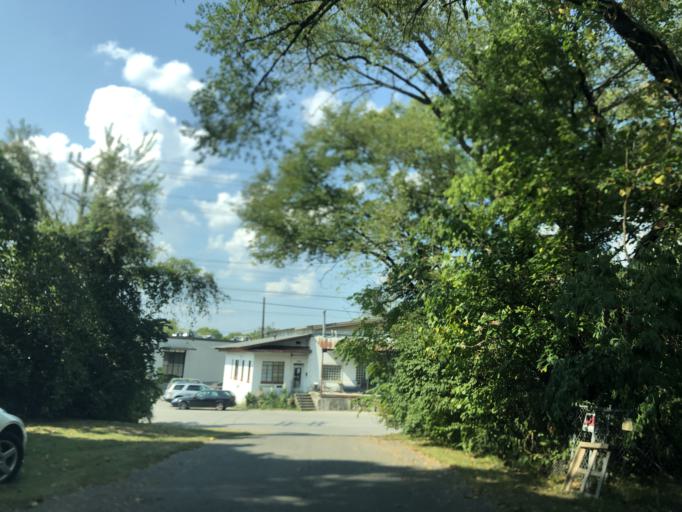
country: US
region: Tennessee
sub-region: Davidson County
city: Oak Hill
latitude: 36.1217
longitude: -86.7693
